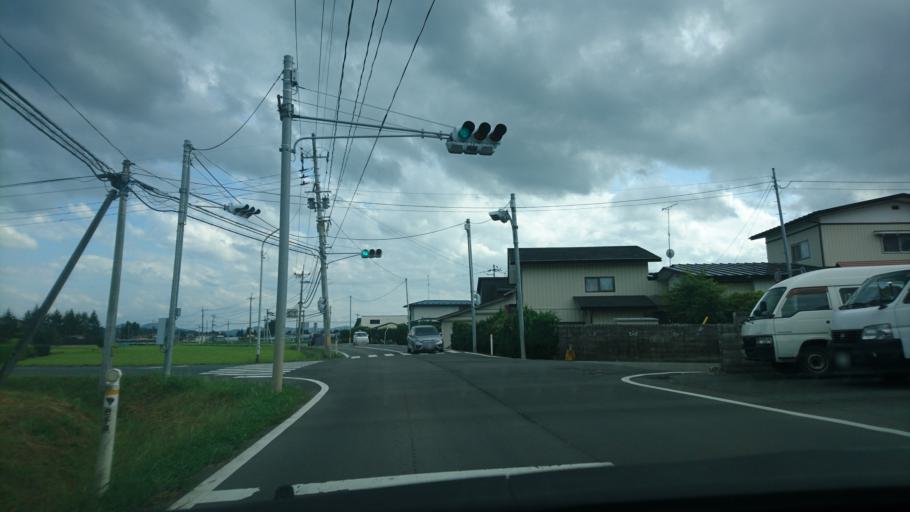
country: JP
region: Iwate
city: Hanamaki
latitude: 39.3673
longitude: 141.1448
